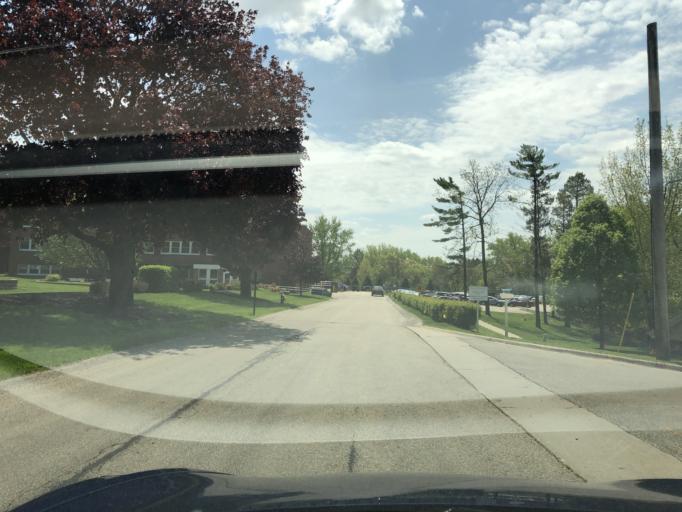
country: US
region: Illinois
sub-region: Jo Daviess County
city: East Dubuque
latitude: 42.4772
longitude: -90.6586
